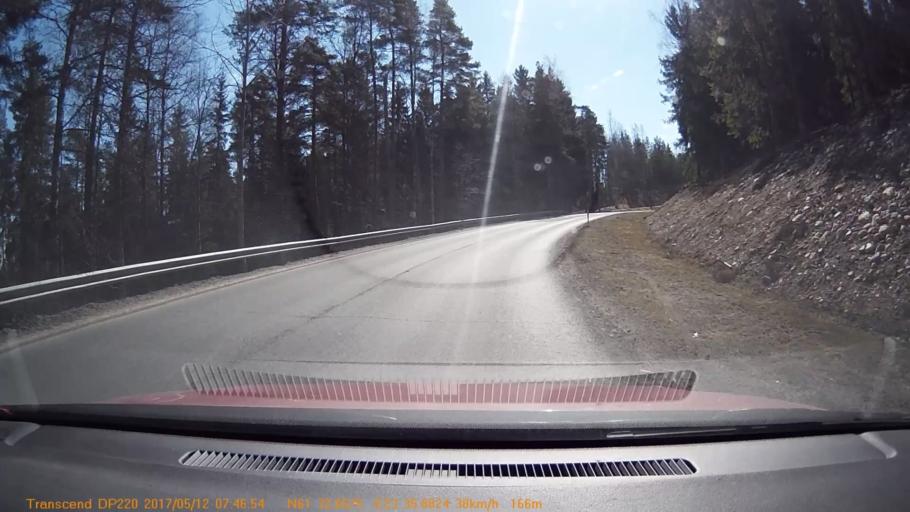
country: FI
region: Pirkanmaa
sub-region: Tampere
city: Yloejaervi
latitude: 61.5443
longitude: 23.5978
